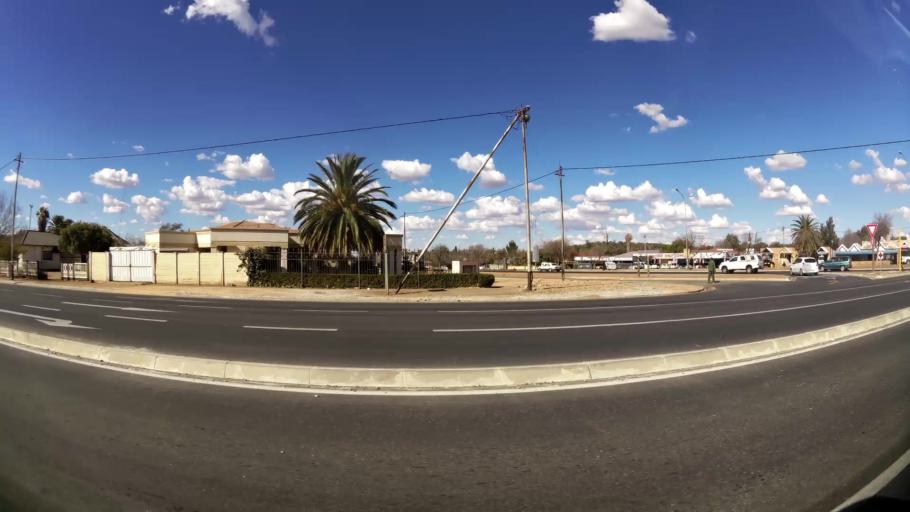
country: ZA
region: North-West
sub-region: Dr Kenneth Kaunda District Municipality
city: Klerksdorp
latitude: -26.8649
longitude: 26.6408
